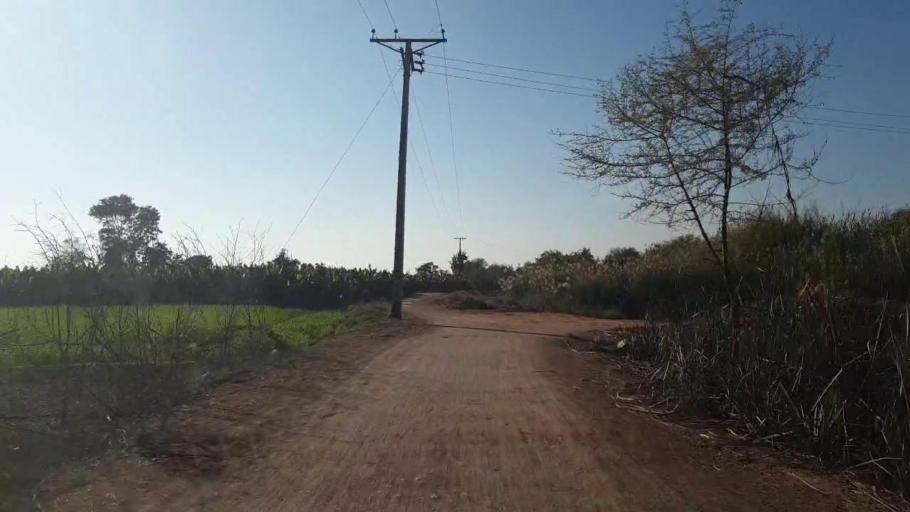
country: PK
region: Sindh
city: Shahdadpur
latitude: 25.9287
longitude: 68.5918
